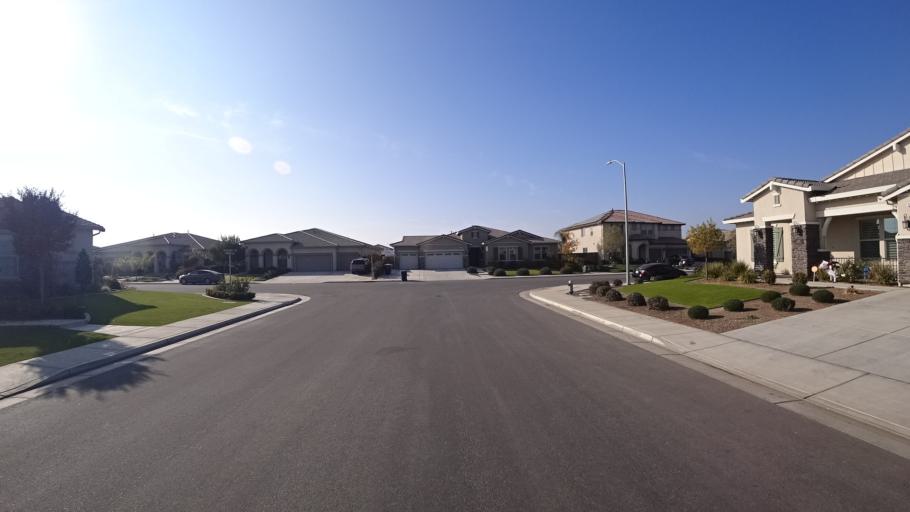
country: US
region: California
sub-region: Kern County
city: Rosedale
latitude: 35.3484
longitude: -119.1722
